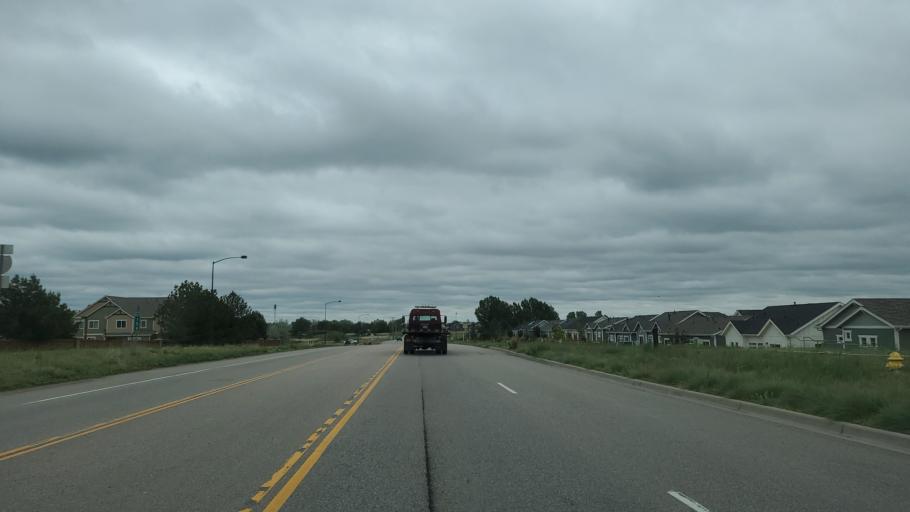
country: US
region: Colorado
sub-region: Adams County
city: Brighton
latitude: 39.9143
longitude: -104.8029
